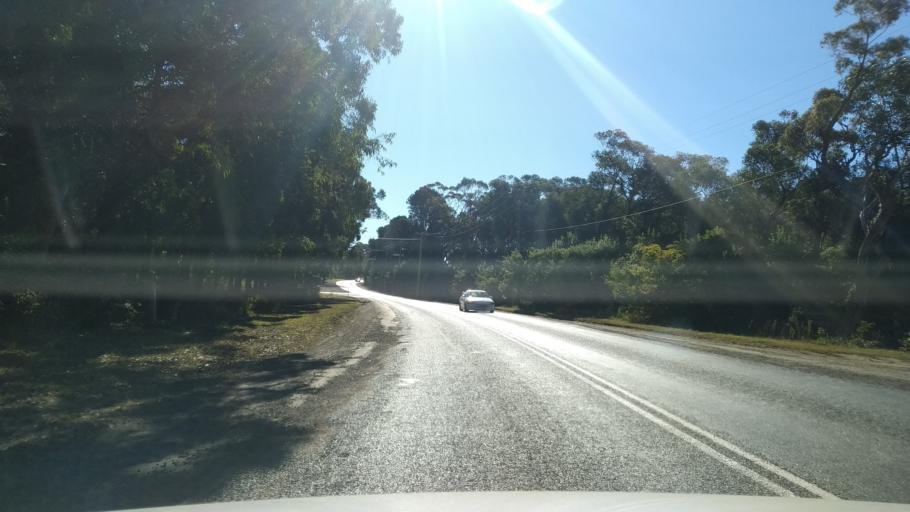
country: AU
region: New South Wales
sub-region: Wyong Shire
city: Little Jilliby
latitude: -33.2665
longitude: 151.2160
